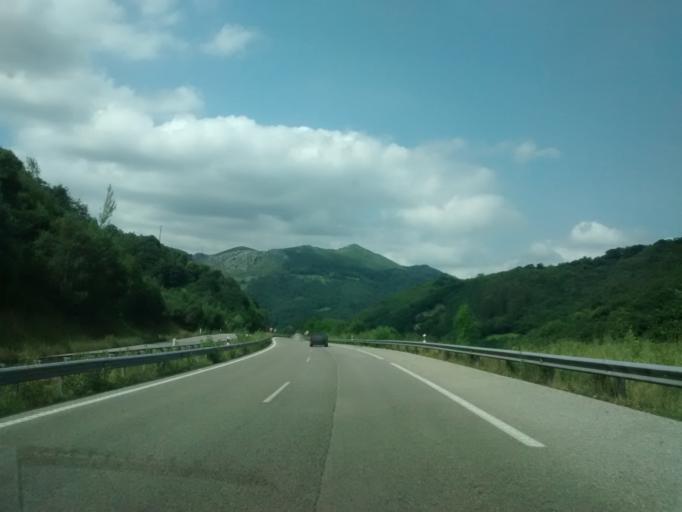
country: ES
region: Asturias
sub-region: Province of Asturias
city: Mieres
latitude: 43.3088
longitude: -5.7465
